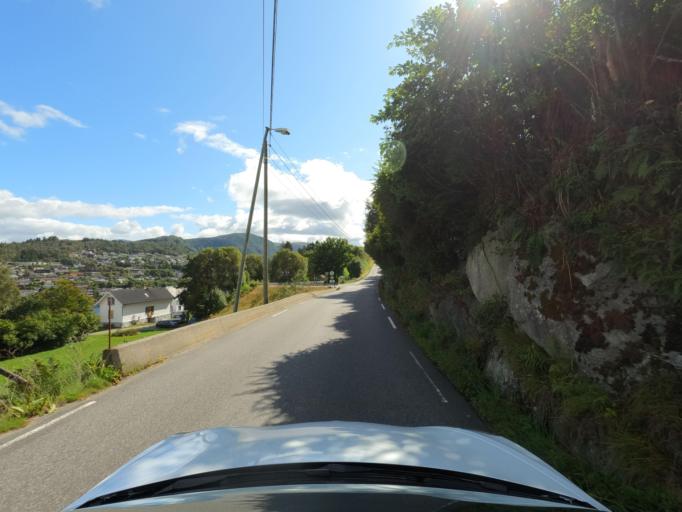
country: NO
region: Hordaland
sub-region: Bergen
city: Ytre Arna
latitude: 60.4467
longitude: 5.4499
